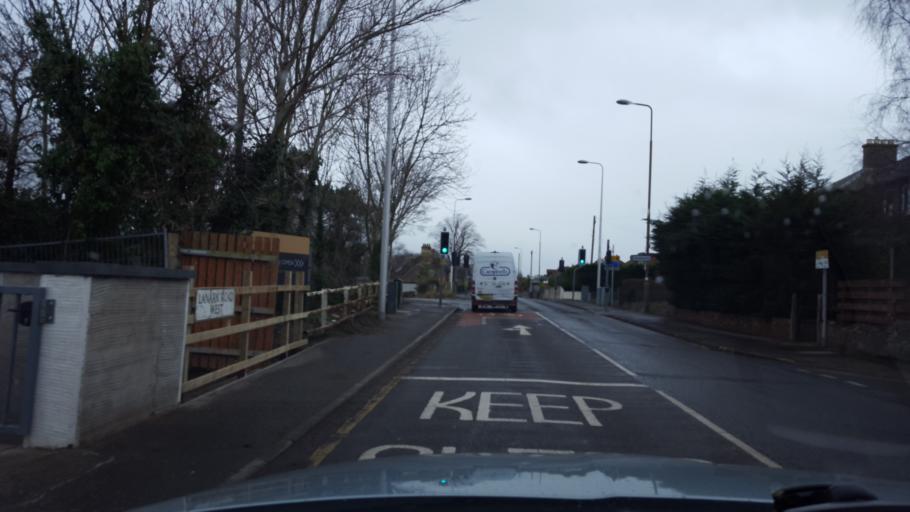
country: GB
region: Scotland
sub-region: Edinburgh
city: Currie
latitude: 55.9007
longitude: -3.2933
